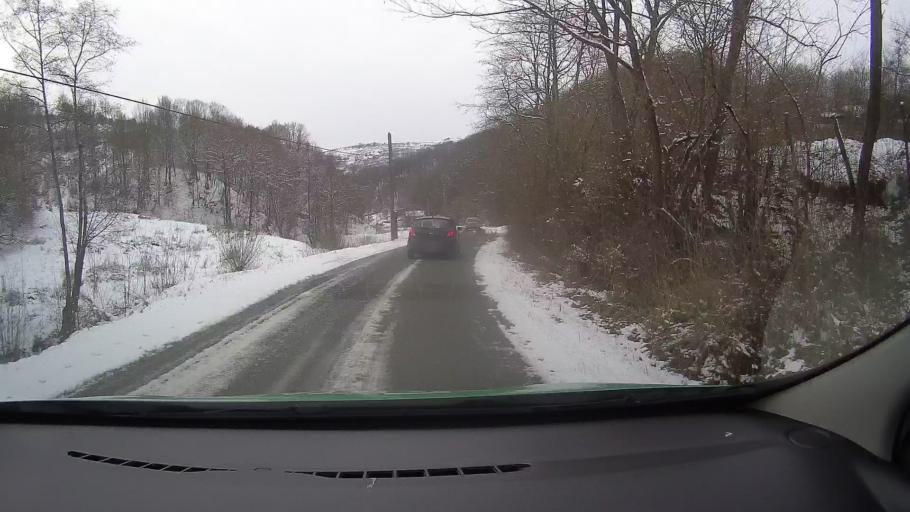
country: RO
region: Alba
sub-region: Comuna Almasu Mare
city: Almasu Mare
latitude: 46.0784
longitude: 23.1131
